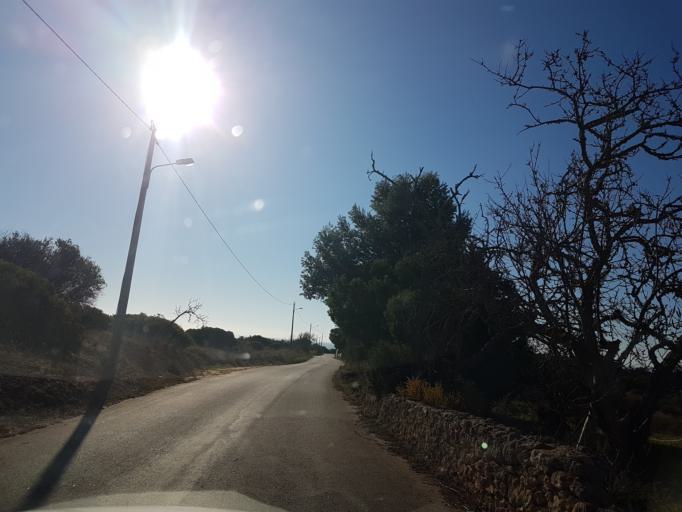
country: PT
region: Faro
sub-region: Lagoa
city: Carvoeiro
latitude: 37.0949
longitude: -8.4196
